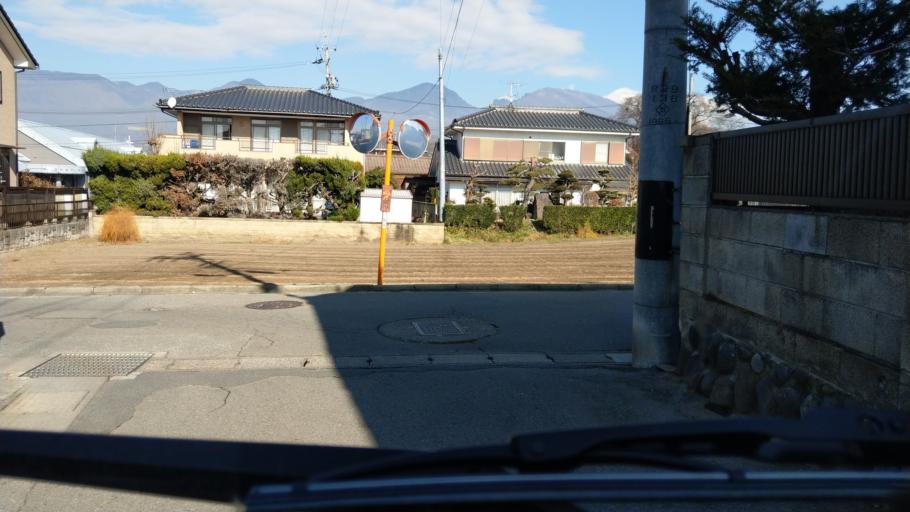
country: JP
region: Nagano
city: Komoro
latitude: 36.3143
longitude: 138.4331
